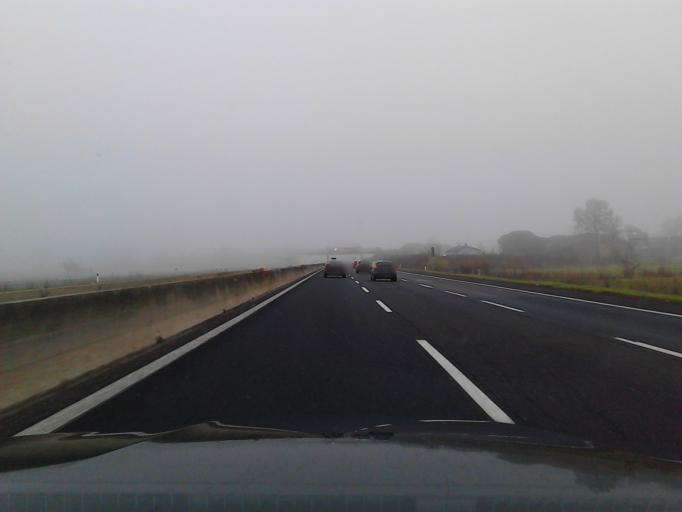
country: IT
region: Emilia-Romagna
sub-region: Forli-Cesena
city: Santa Maria Nuova
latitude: 44.2027
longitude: 12.2062
